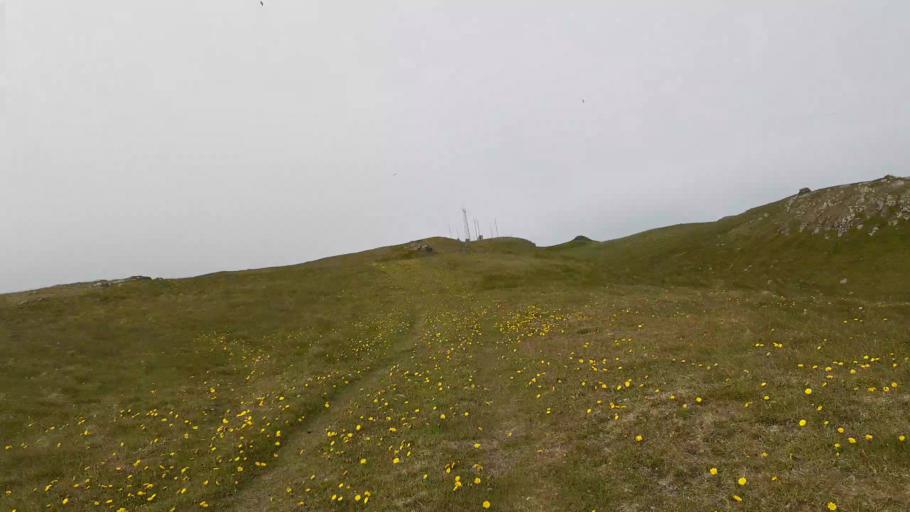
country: IS
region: Northeast
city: Dalvik
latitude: 66.5419
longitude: -17.9918
